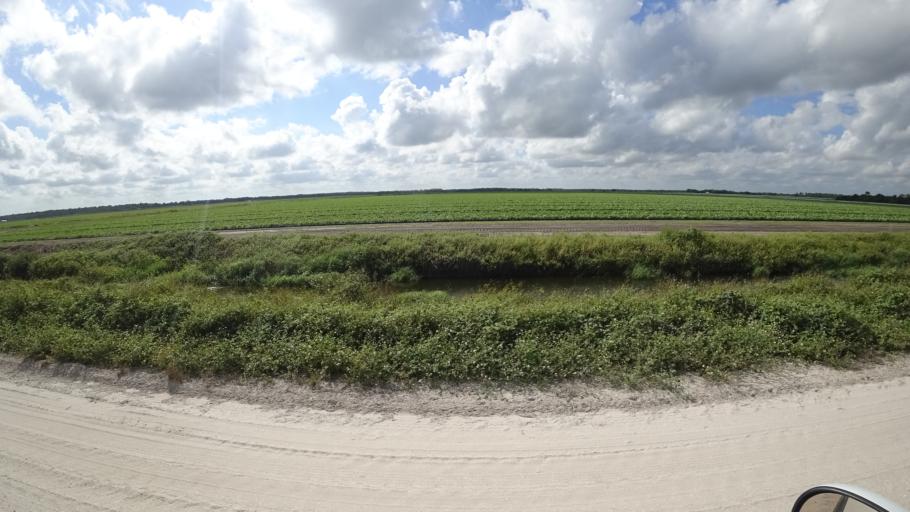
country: US
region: Florida
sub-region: Sarasota County
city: Lake Sarasota
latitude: 27.4131
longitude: -82.2085
